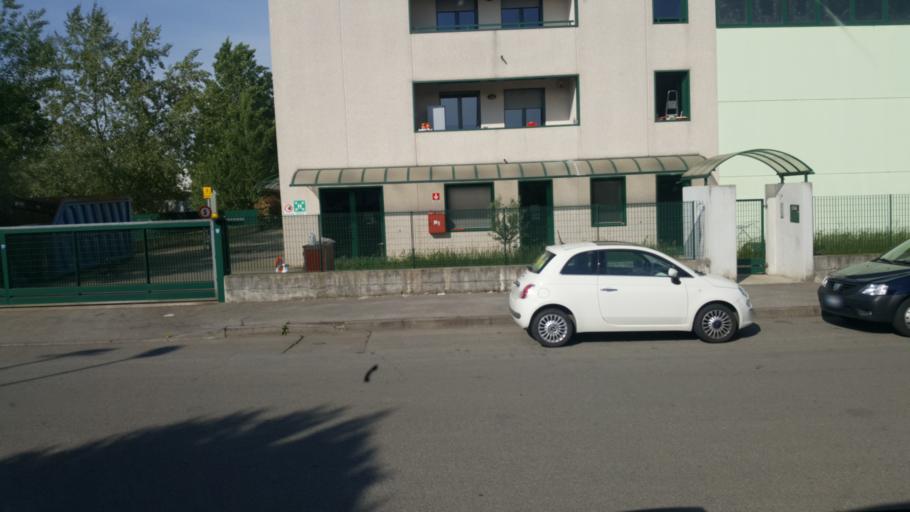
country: IT
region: Lombardy
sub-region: Citta metropolitana di Milano
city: Liscate
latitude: 45.4887
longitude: 9.4121
